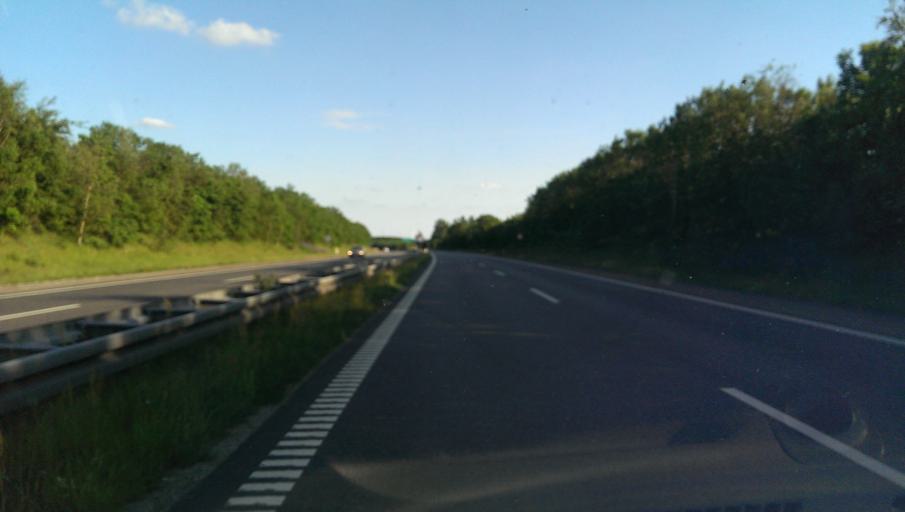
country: DK
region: South Denmark
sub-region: Esbjerg Kommune
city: Esbjerg
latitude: 55.4916
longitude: 8.5029
